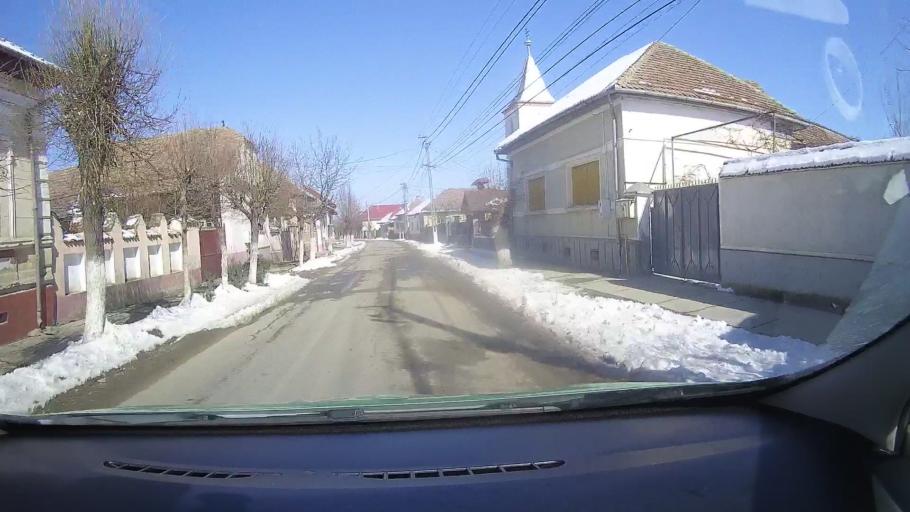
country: RO
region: Brasov
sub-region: Comuna Mandra
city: Mandra
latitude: 45.8166
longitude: 25.0037
